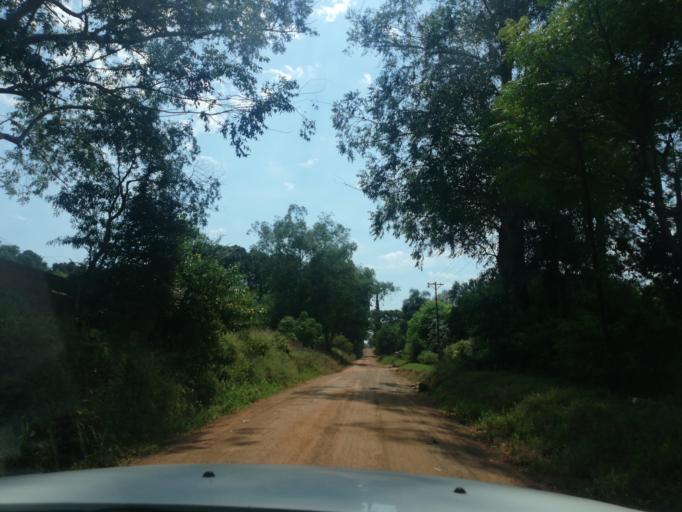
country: AR
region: Misiones
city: Garupa
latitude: -27.4428
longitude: -55.8889
